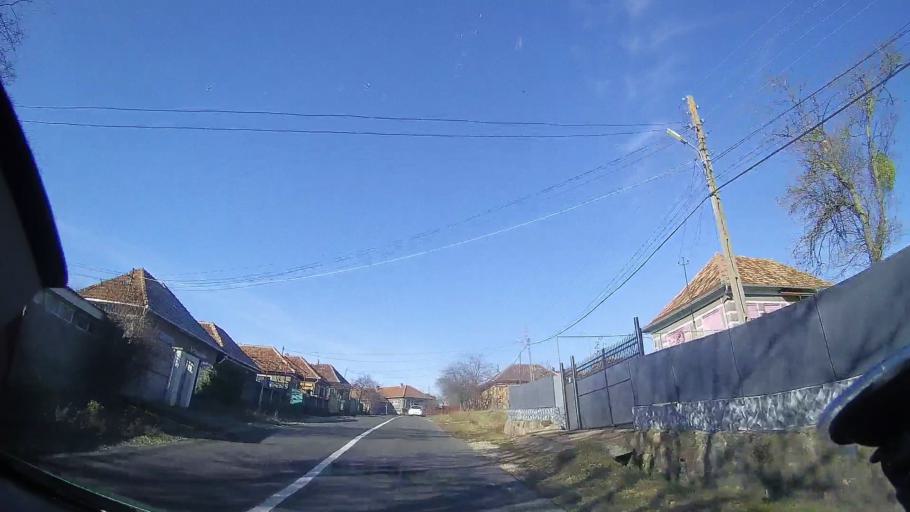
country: RO
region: Bihor
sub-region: Comuna Bratca
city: Beznea
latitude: 46.9604
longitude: 22.6171
